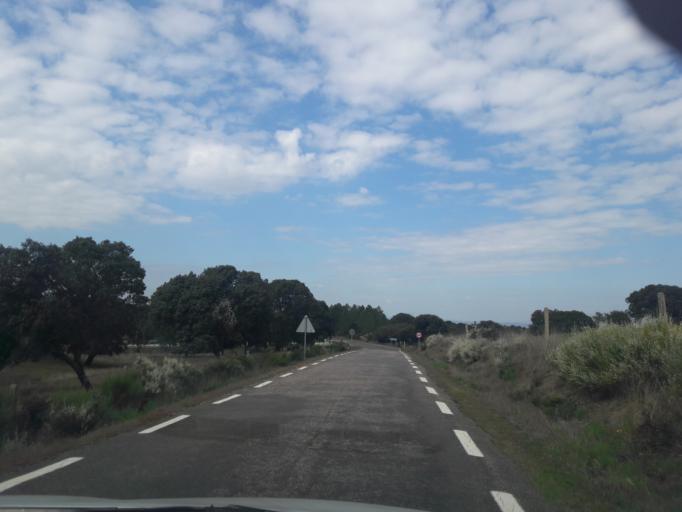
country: ES
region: Castille and Leon
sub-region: Provincia de Salamanca
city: Zamarra
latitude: 40.5452
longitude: -6.4185
